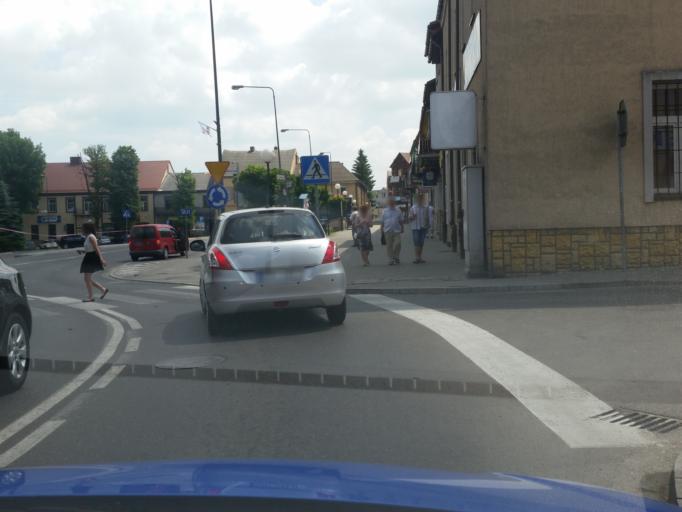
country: PL
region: Lesser Poland Voivodeship
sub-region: Powiat miechowski
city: Miechow
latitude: 50.3562
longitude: 20.0269
